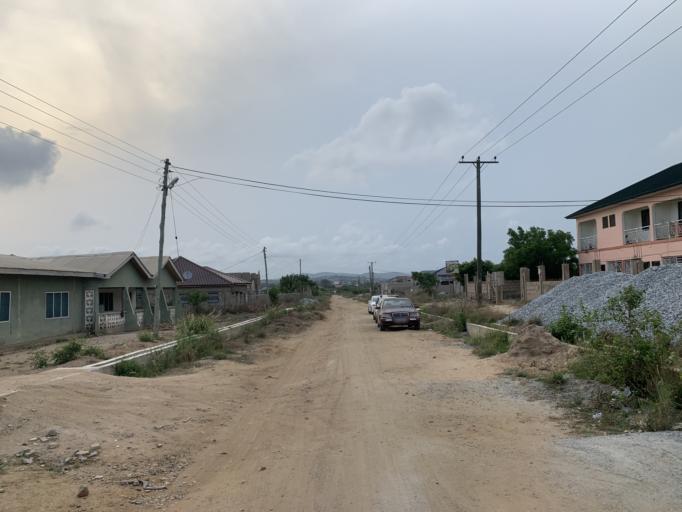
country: GH
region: Central
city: Winneba
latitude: 5.3834
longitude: -0.6292
